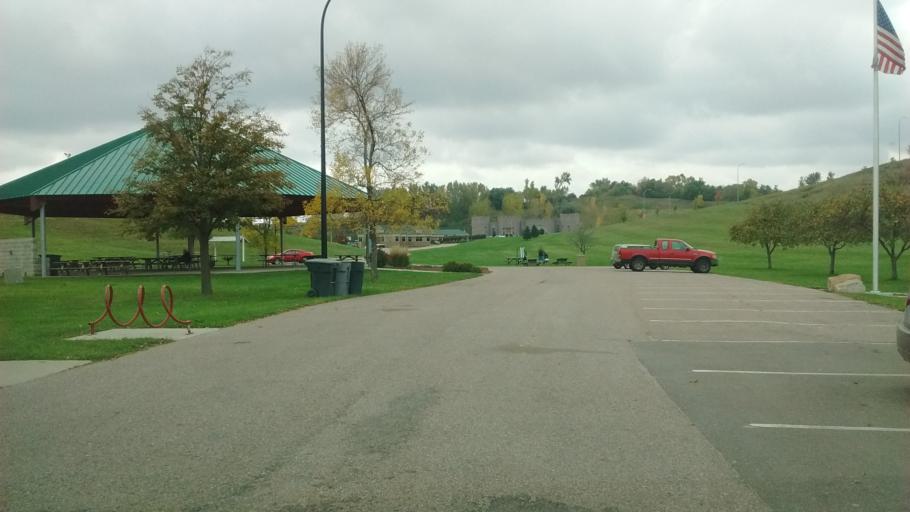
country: US
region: Iowa
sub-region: Woodbury County
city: Sergeant Bluff
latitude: 42.4410
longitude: -96.3521
